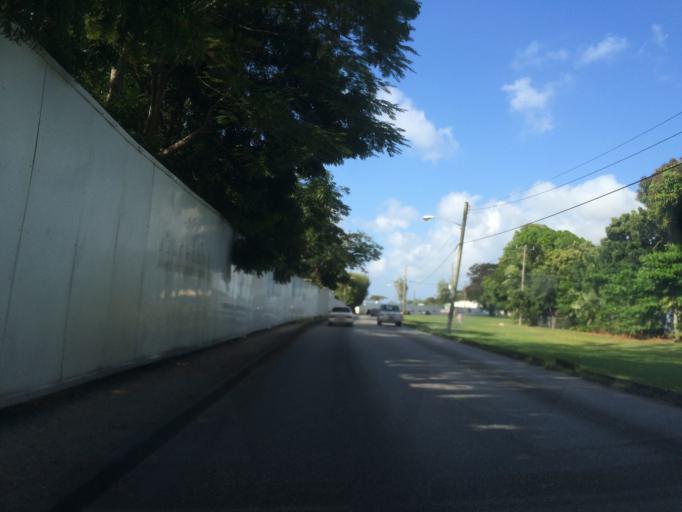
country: BB
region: Saint James
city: Holetown
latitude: 13.1796
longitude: -59.6385
